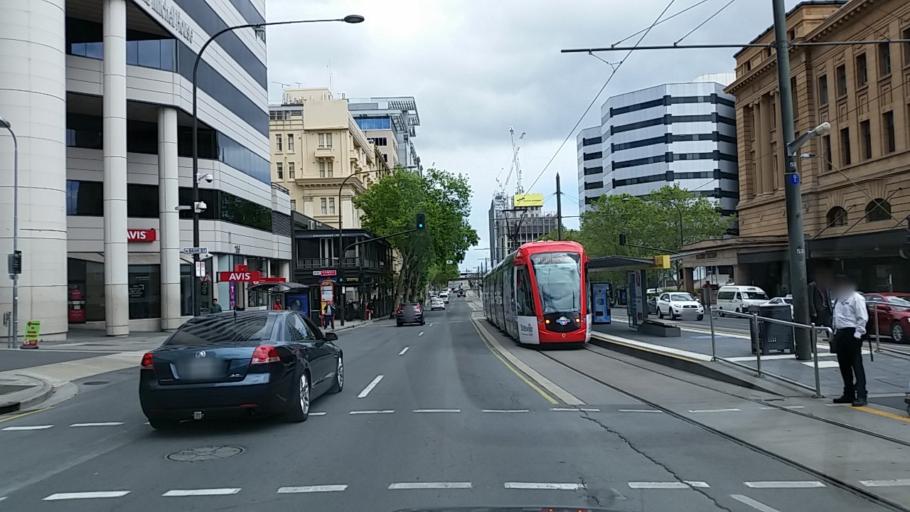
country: AU
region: South Australia
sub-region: Adelaide
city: Adelaide
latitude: -34.9217
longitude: 138.5977
